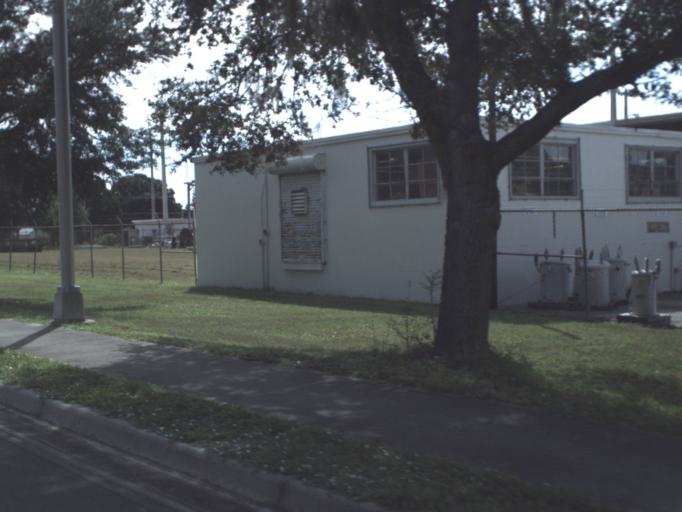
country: US
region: Florida
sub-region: DeSoto County
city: Arcadia
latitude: 27.2196
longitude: -81.8585
